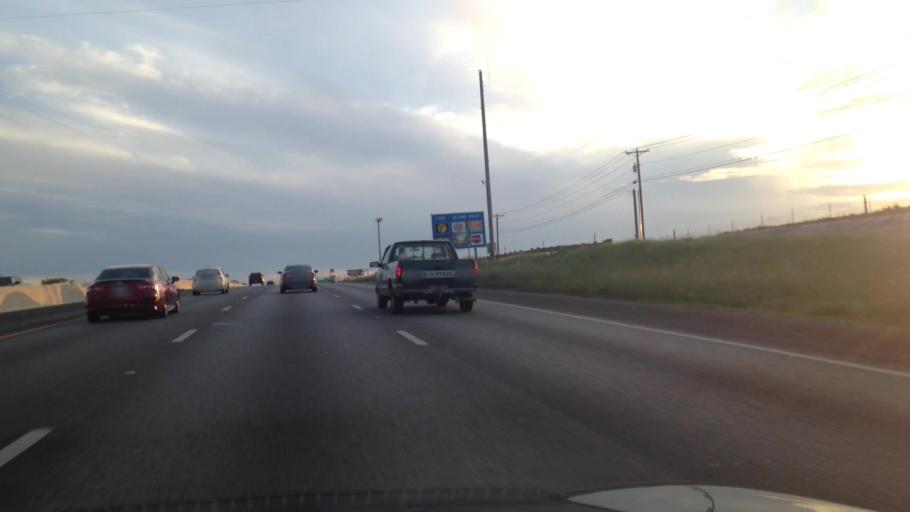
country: US
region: Texas
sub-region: Guadalupe County
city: Lake Dunlap
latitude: 29.7590
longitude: -98.0492
